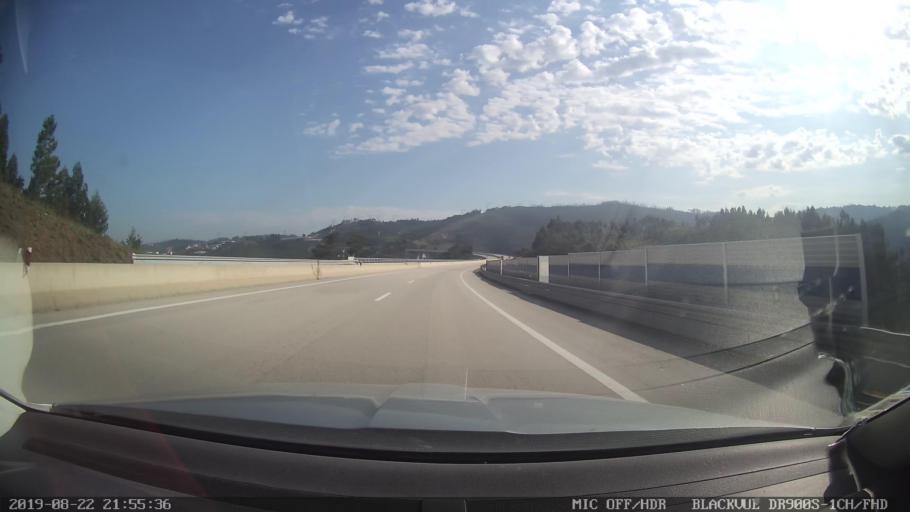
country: PT
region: Coimbra
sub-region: Coimbra
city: Coimbra
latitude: 40.1554
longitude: -8.3842
